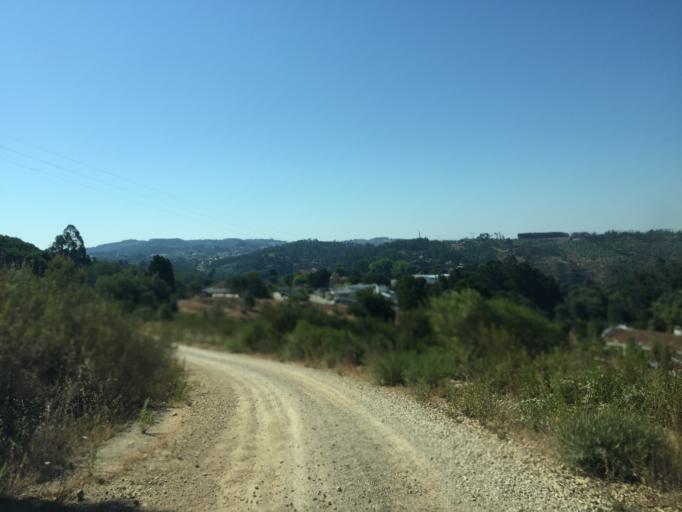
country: PT
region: Santarem
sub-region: Constancia
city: Constancia
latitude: 39.5507
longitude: -8.3248
